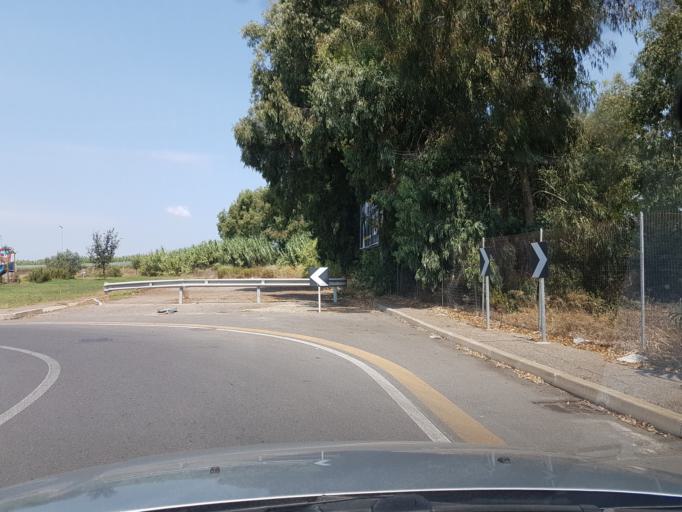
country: IT
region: Sardinia
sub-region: Provincia di Oristano
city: Oristano
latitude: 39.9153
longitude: 8.5883
